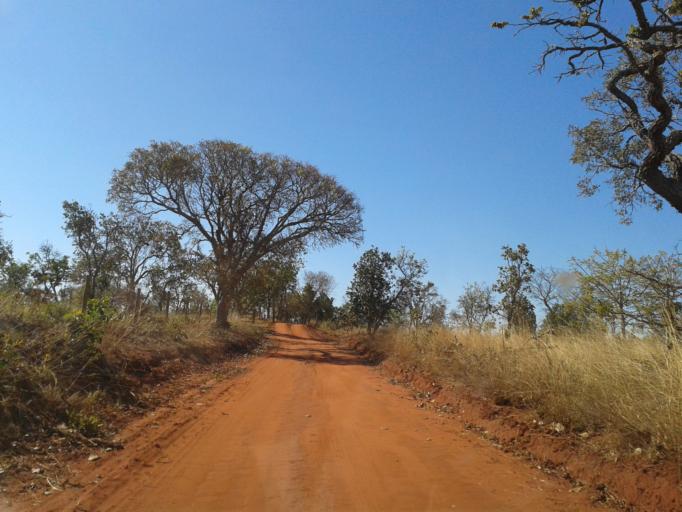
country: BR
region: Minas Gerais
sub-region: Ituiutaba
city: Ituiutaba
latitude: -19.0821
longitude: -49.3373
